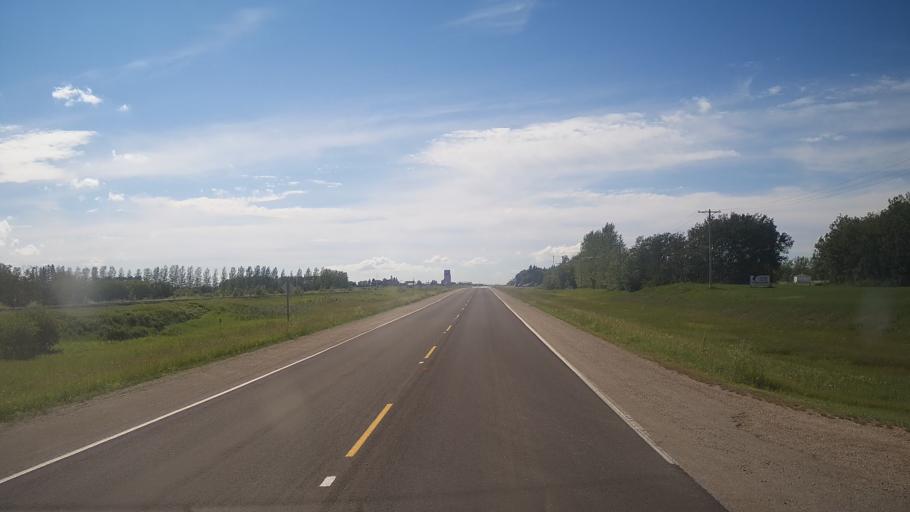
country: CA
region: Saskatchewan
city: Foam Lake
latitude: 51.2585
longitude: -103.7236
